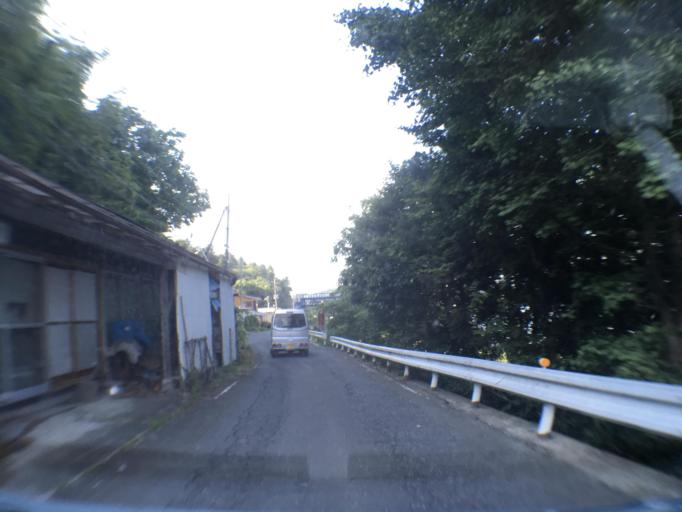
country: JP
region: Miyagi
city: Wakuya
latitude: 38.6471
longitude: 141.2818
